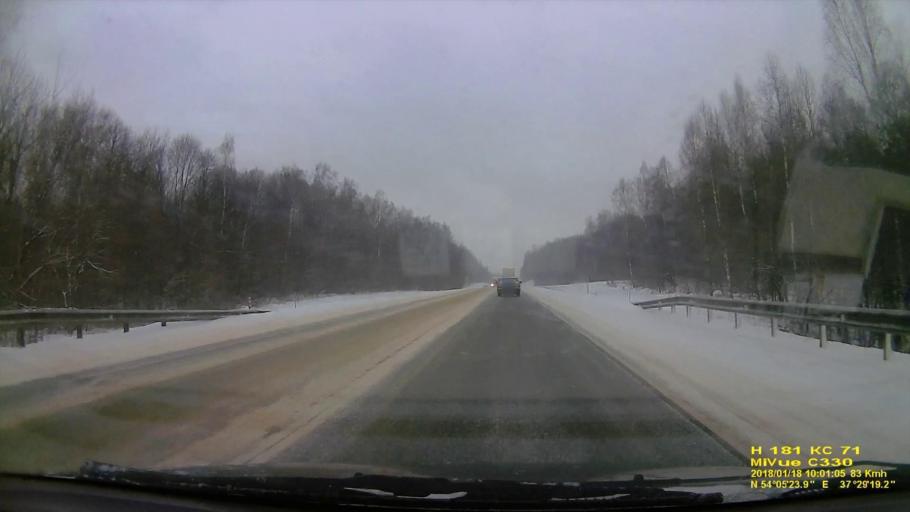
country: RU
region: Tula
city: Pervomayskiy
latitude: 54.0900
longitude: 37.4887
